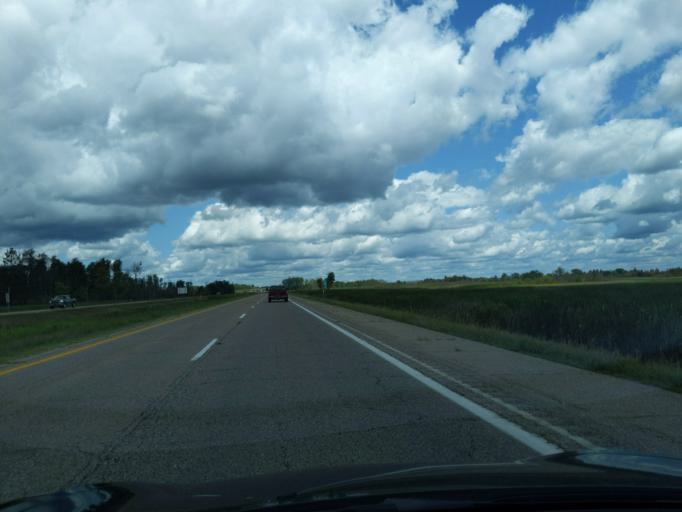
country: US
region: Michigan
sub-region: Roscommon County
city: Houghton Lake
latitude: 44.3600
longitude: -84.8076
